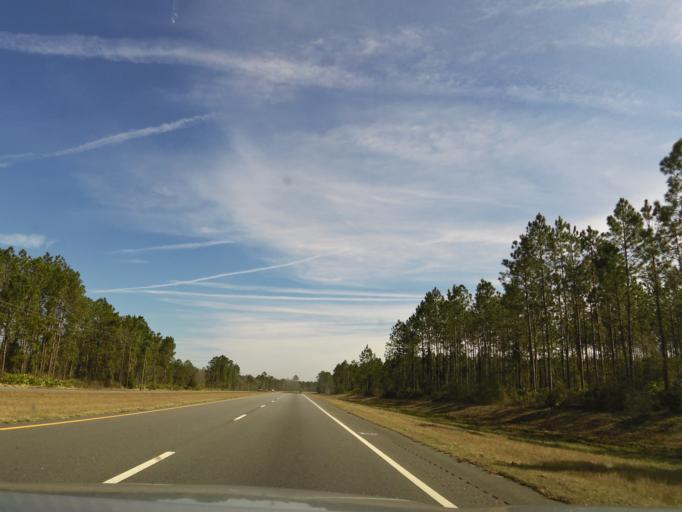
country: US
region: Georgia
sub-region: Brantley County
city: Nahunta
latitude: 31.2134
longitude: -81.9166
